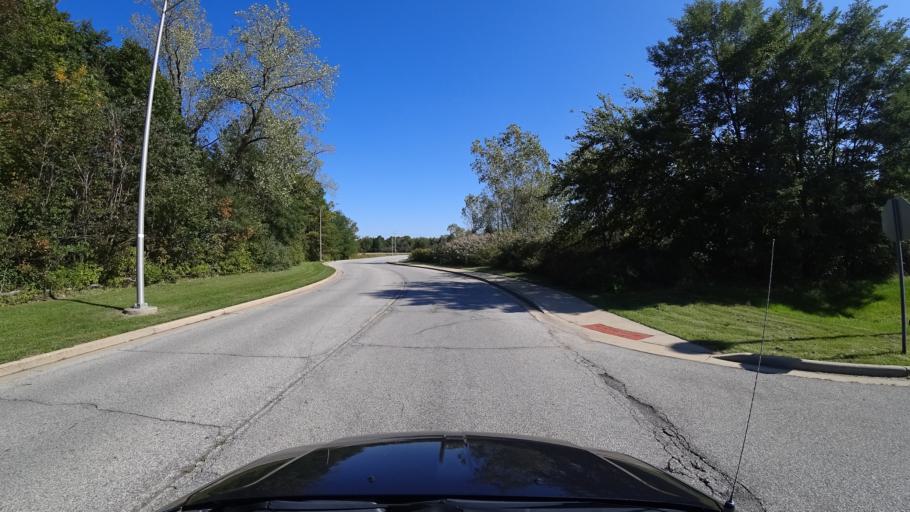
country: US
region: Indiana
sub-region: LaPorte County
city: Michigan City
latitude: 41.6747
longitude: -86.8868
